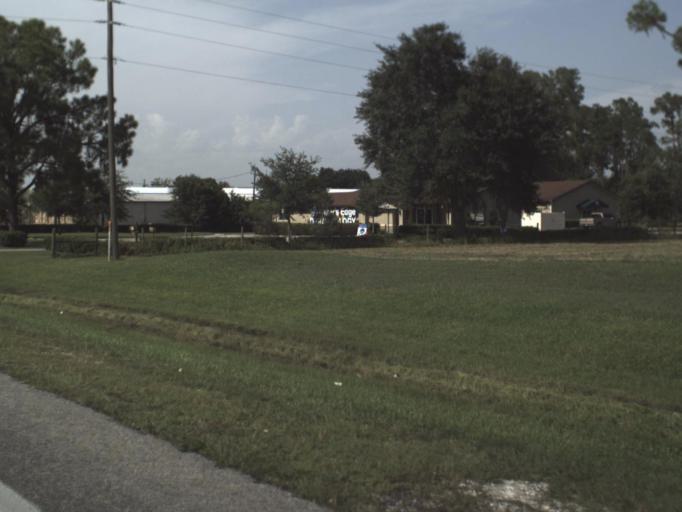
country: US
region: Florida
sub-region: Polk County
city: Lake Wales
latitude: 27.9391
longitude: -81.6123
